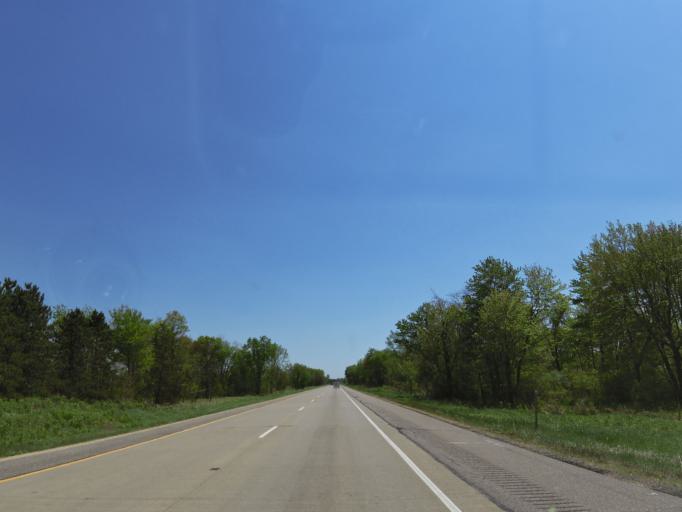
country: US
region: Wisconsin
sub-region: Juneau County
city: New Lisbon
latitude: 43.8561
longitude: -90.1106
